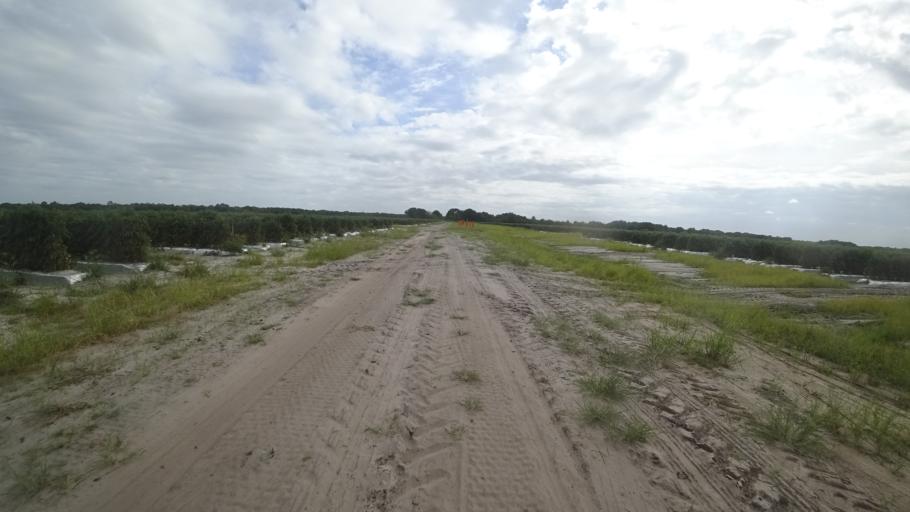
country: US
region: Florida
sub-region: Hillsborough County
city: Wimauma
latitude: 27.5859
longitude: -82.3104
